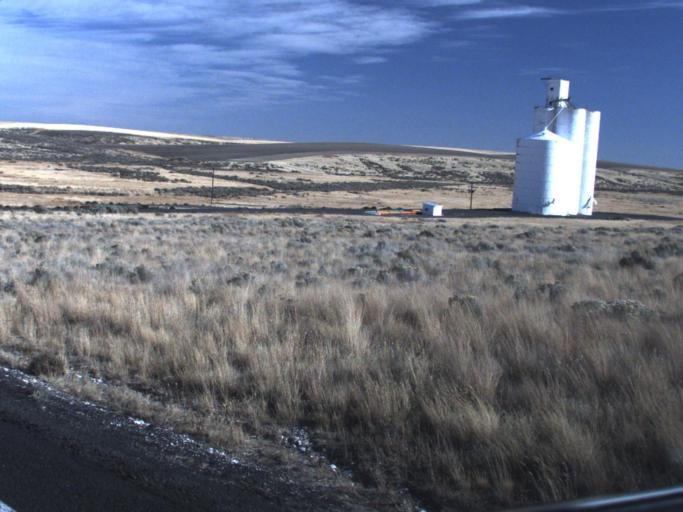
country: US
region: Washington
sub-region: Adams County
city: Ritzville
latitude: 47.2229
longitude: -118.6863
